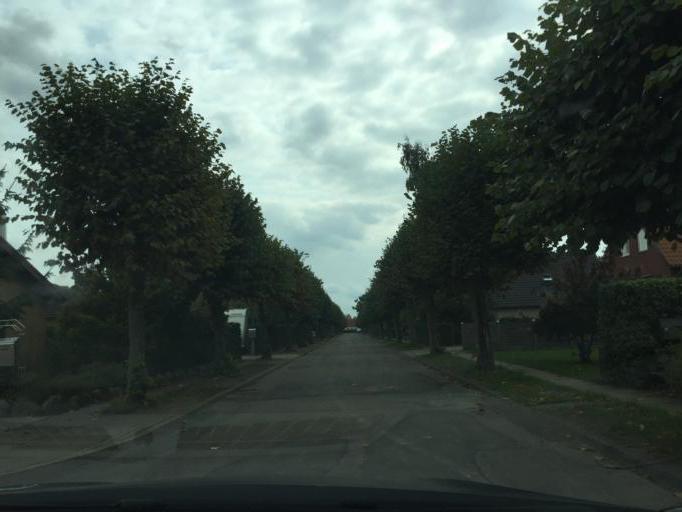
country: DK
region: South Denmark
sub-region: Odense Kommune
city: Stige
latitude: 55.4393
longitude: 10.4146
